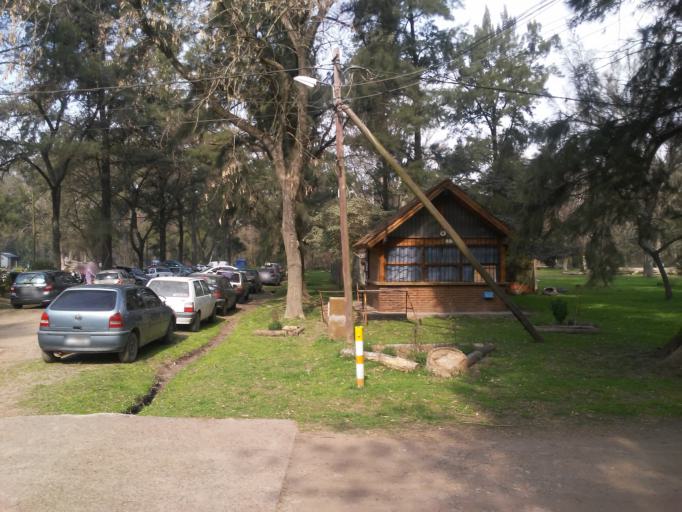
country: AR
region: Buenos Aires
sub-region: Partido de General Rodriguez
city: General Rodriguez
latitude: -34.6655
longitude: -58.8571
